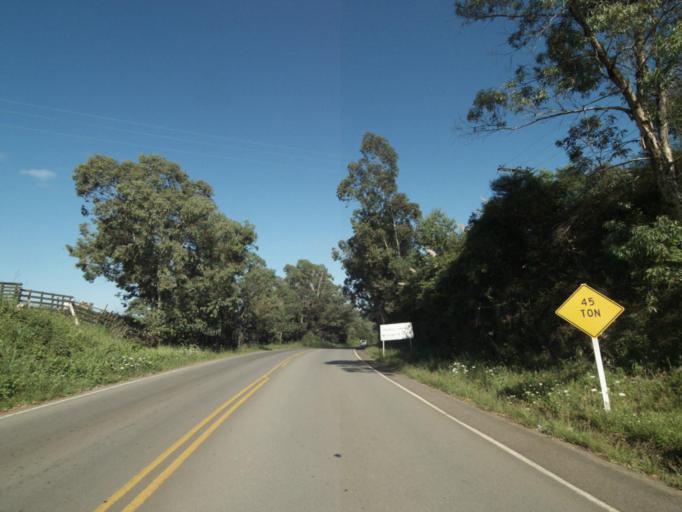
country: BR
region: Rio Grande do Sul
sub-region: Bento Goncalves
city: Bento Goncalves
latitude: -29.1214
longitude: -51.5474
